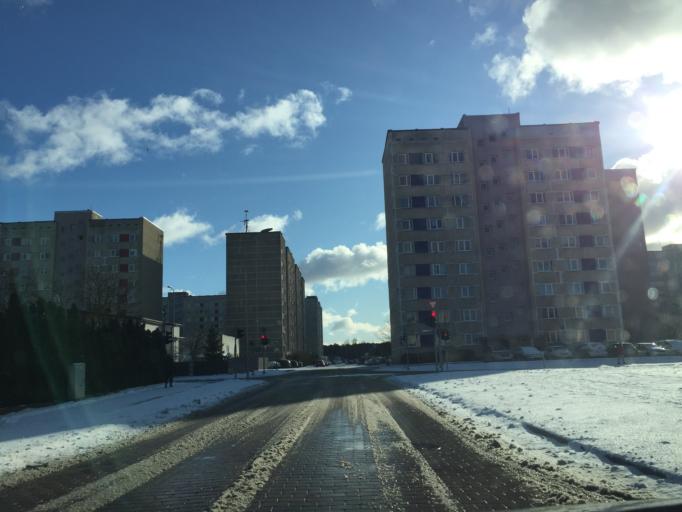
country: LV
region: Ventspils
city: Ventspils
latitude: 57.3849
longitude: 21.5508
